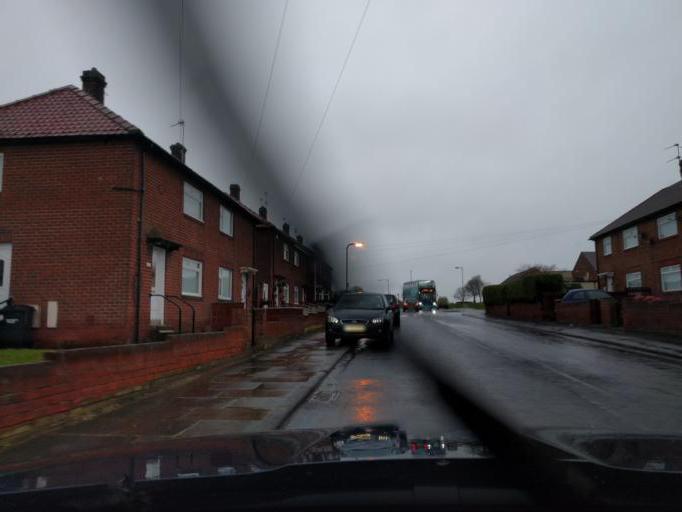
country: GB
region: England
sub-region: Northumberland
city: Newbiggin-by-the-Sea
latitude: 55.1870
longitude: -1.5139
